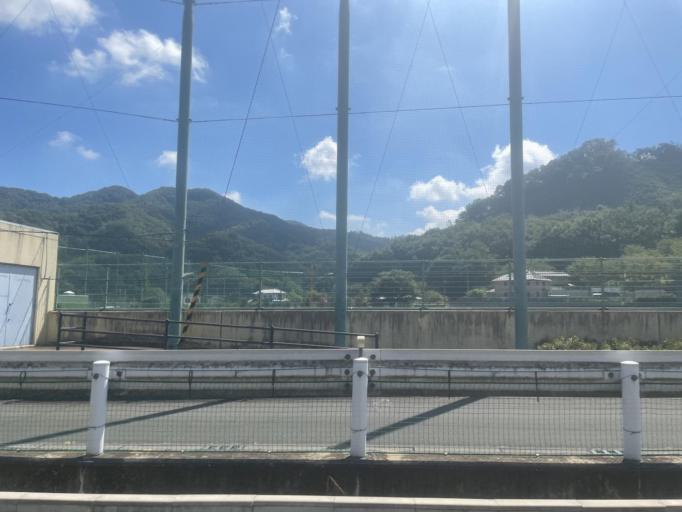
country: JP
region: Saitama
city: Yorii
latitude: 36.0818
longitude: 139.1155
